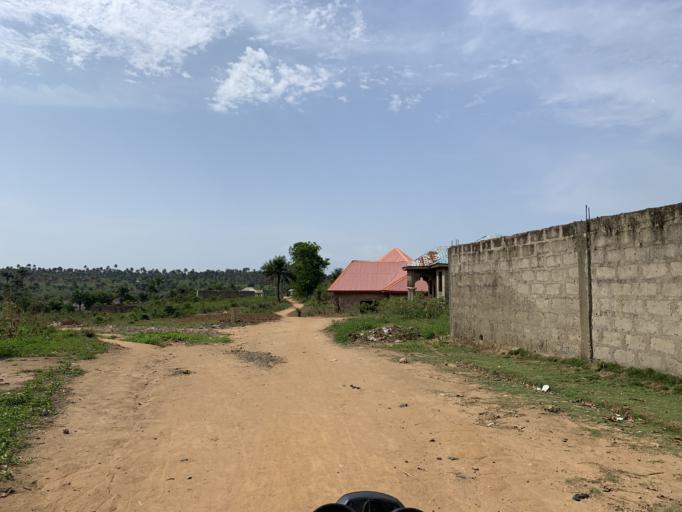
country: SL
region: Western Area
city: Waterloo
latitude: 8.3467
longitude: -13.0528
